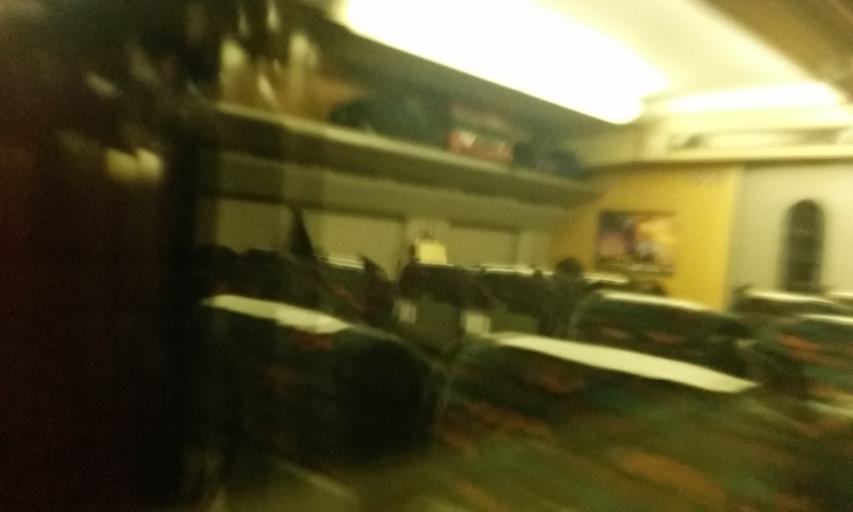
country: JP
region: Miyagi
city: Iwanuma
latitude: 38.1331
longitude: 140.8107
